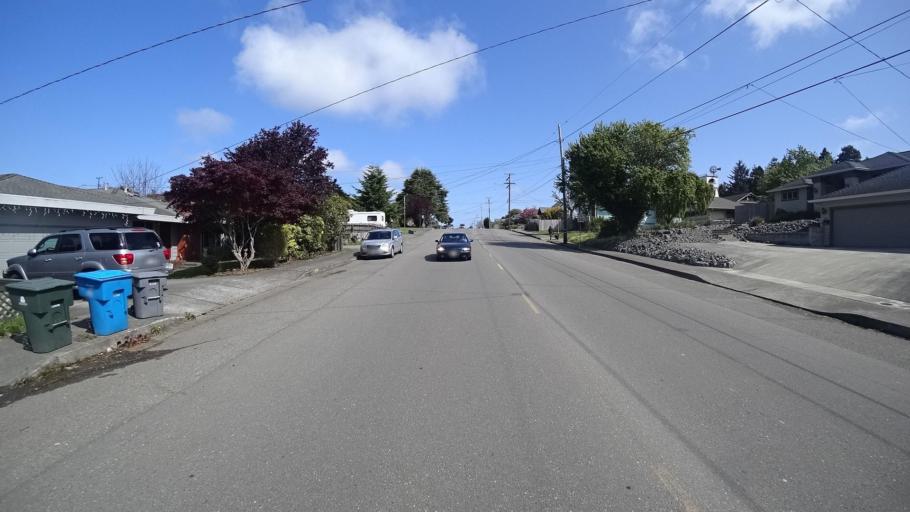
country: US
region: California
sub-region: Humboldt County
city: Cutten
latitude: 40.7754
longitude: -124.1614
